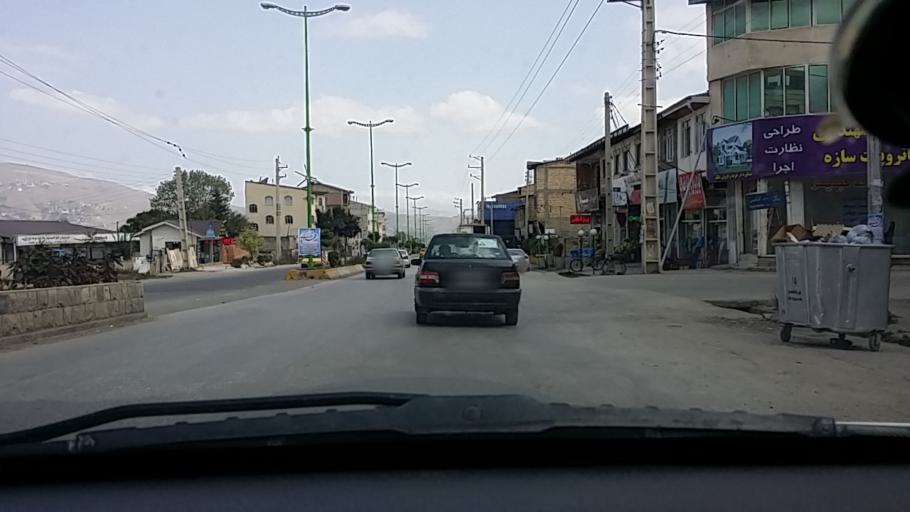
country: IR
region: Mazandaran
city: `Abbasabad
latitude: 36.5076
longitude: 51.1723
